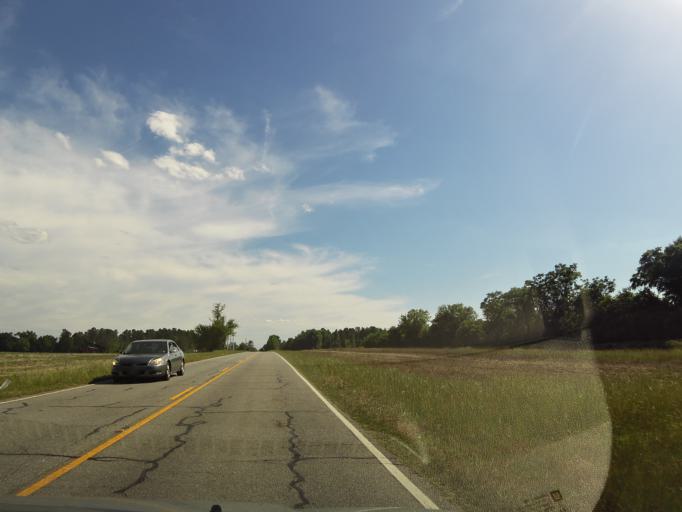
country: US
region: South Carolina
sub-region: Bamberg County
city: Denmark
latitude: 33.1928
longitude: -81.1808
